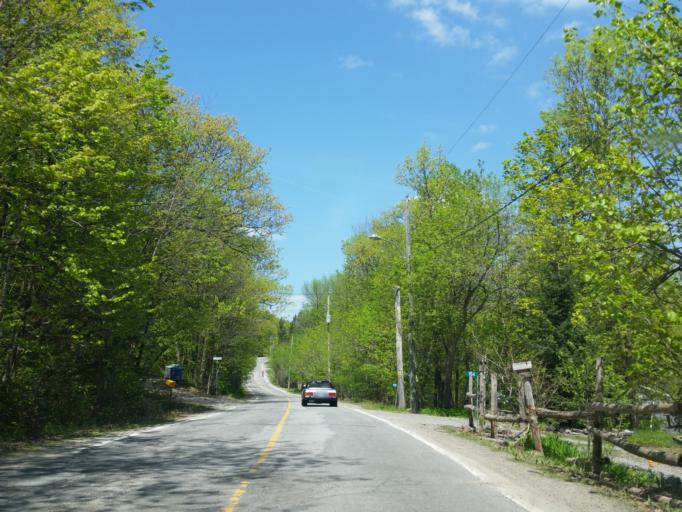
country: CA
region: Quebec
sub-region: Outaouais
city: Wakefield
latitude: 45.5899
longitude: -75.8714
